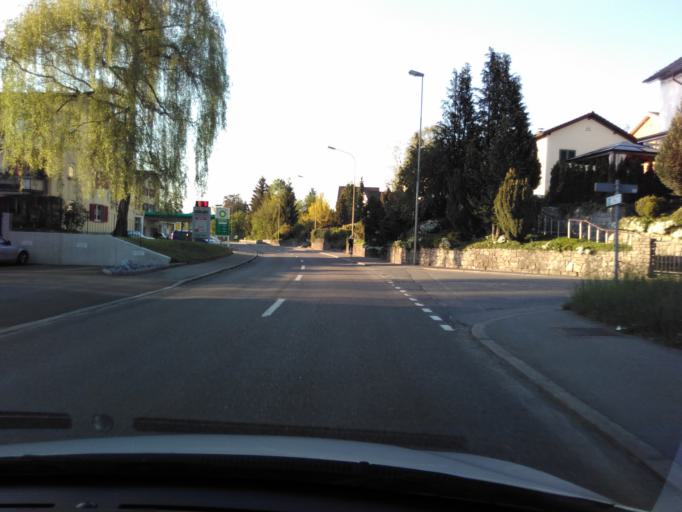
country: CH
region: Zurich
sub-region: Bezirk Hinwil
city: Tann
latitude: 47.2689
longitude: 8.8532
